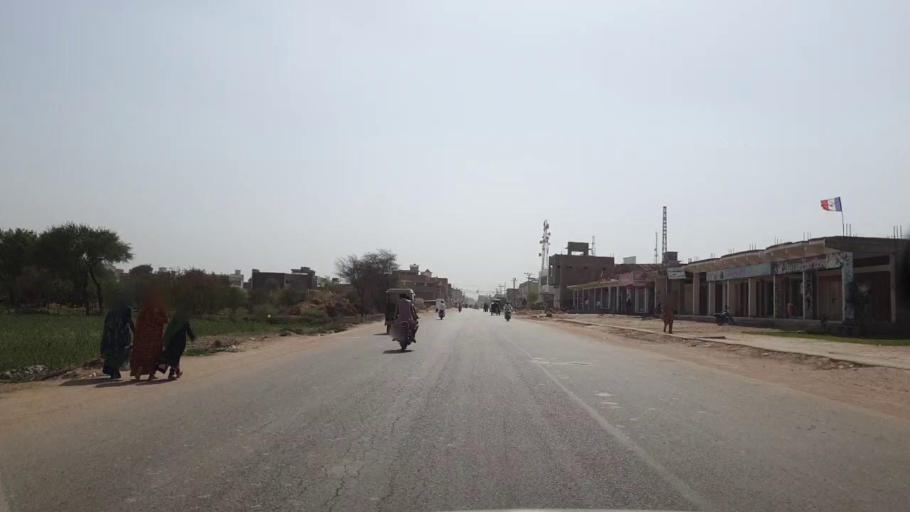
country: PK
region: Sindh
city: Matli
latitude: 25.0498
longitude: 68.6500
